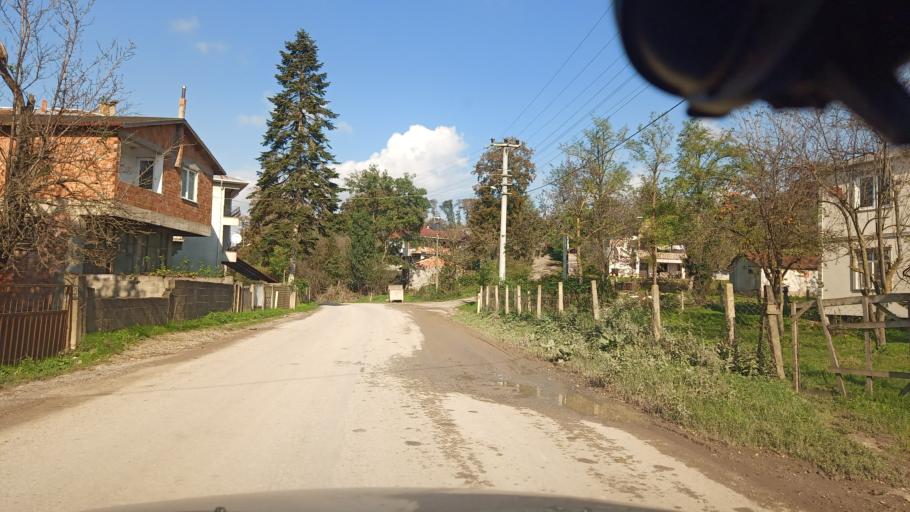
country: TR
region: Sakarya
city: Kaynarca
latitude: 41.0928
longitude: 30.4427
